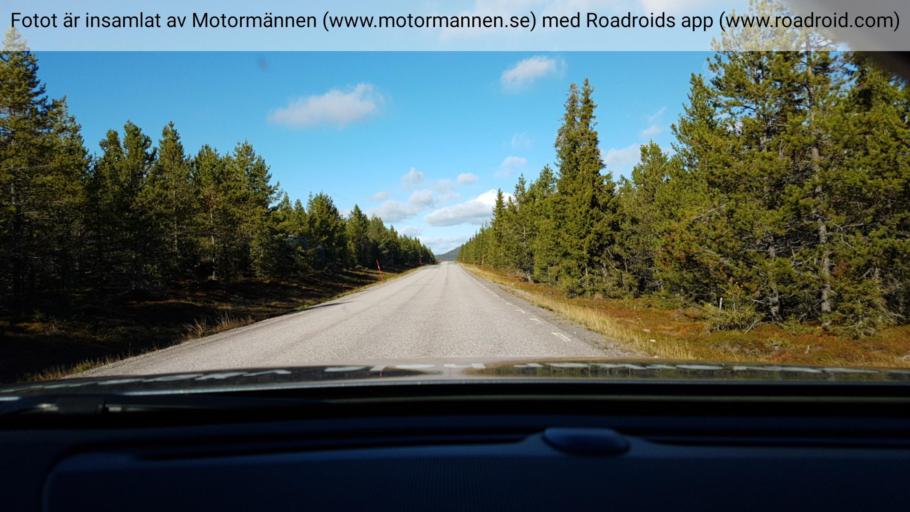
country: SE
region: Norrbotten
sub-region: Arjeplogs Kommun
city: Arjeplog
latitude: 65.8384
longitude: 18.4242
